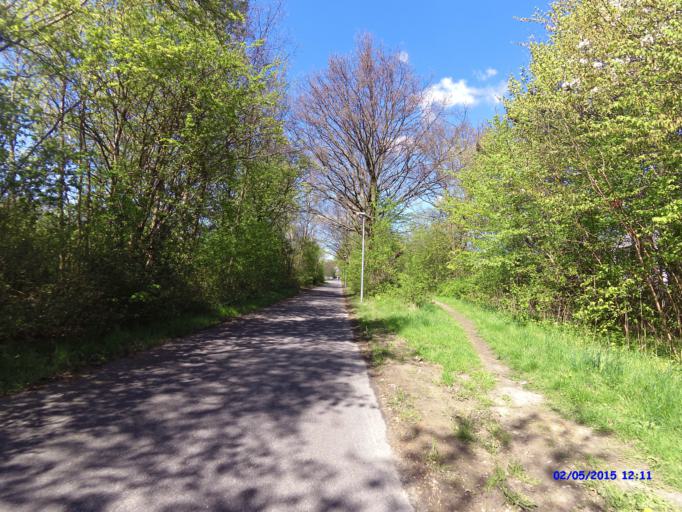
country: DK
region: Capital Region
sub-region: Gladsaxe Municipality
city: Buddinge
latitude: 55.7303
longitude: 12.4761
